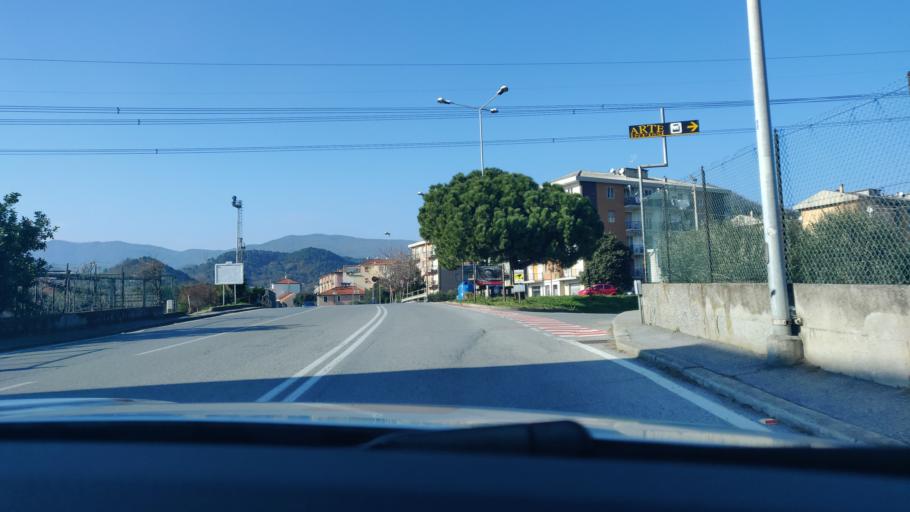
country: IT
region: Liguria
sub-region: Provincia di Savona
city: Quiliano
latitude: 44.2914
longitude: 8.4182
